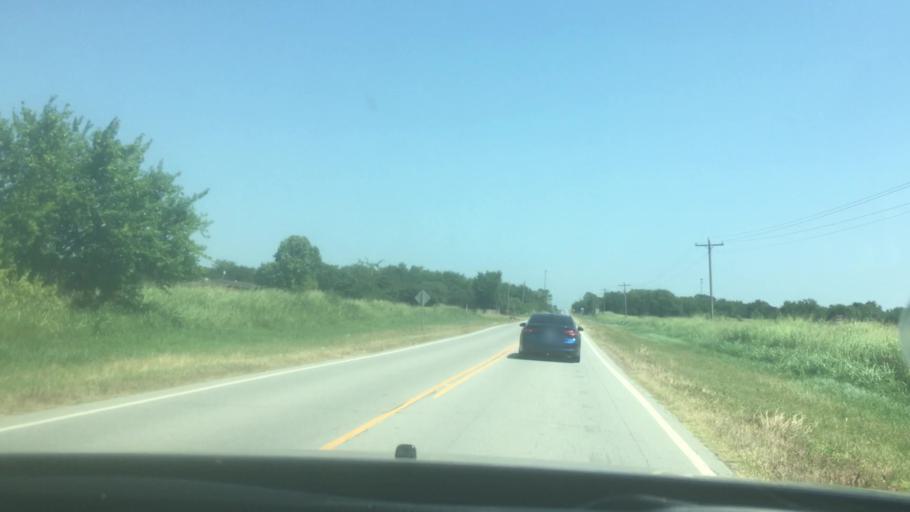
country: US
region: Oklahoma
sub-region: Coal County
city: Coalgate
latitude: 34.5960
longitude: -96.4244
